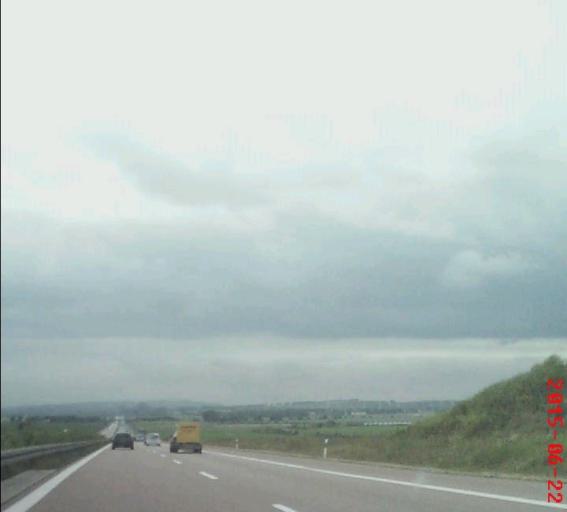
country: DE
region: Saxony-Anhalt
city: Farnstadt
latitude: 51.4470
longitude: 11.5786
